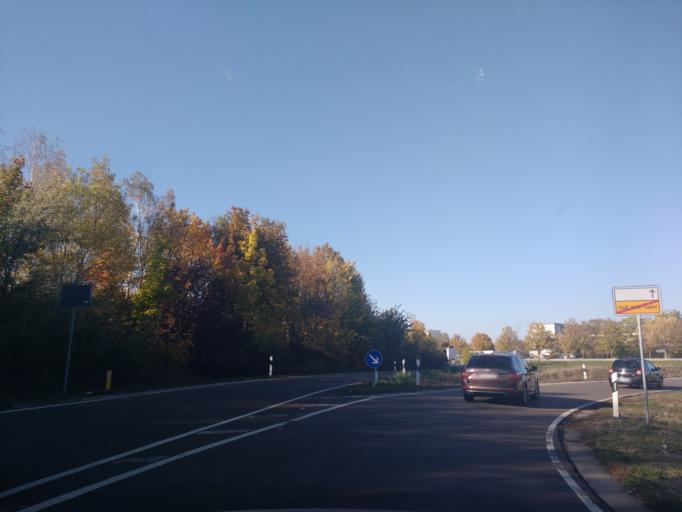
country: DE
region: Saxony-Anhalt
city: Angersdorf
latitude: 51.4735
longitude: 11.8975
